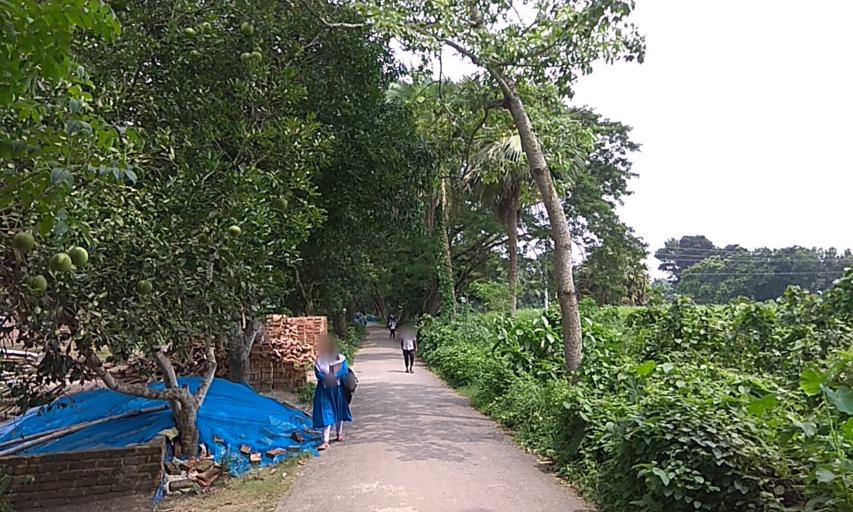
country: BD
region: Dhaka
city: Faridpur
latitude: 23.5349
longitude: 89.9692
